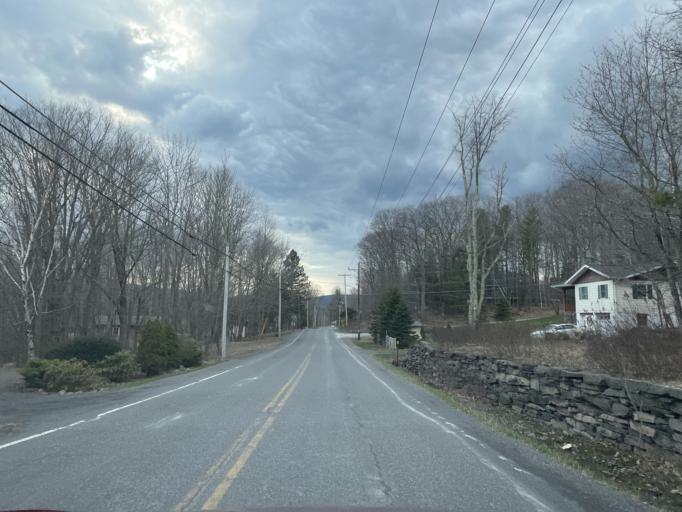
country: US
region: New York
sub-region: Greene County
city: Palenville
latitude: 42.1986
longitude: -74.0802
